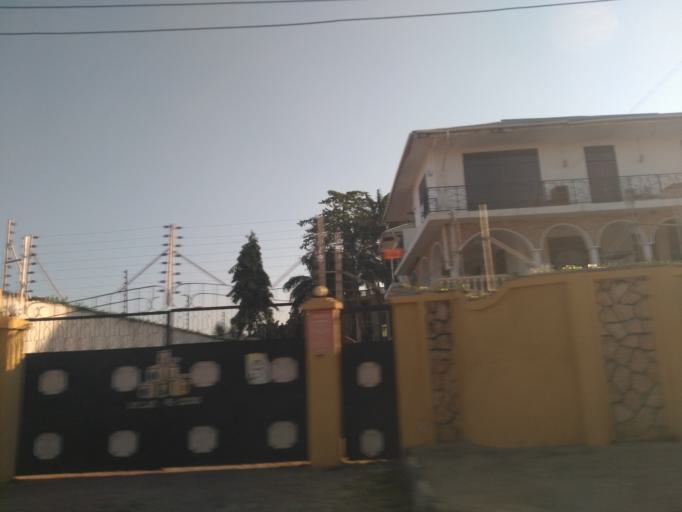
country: TZ
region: Dar es Salaam
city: Magomeni
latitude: -6.7611
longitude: 39.2569
